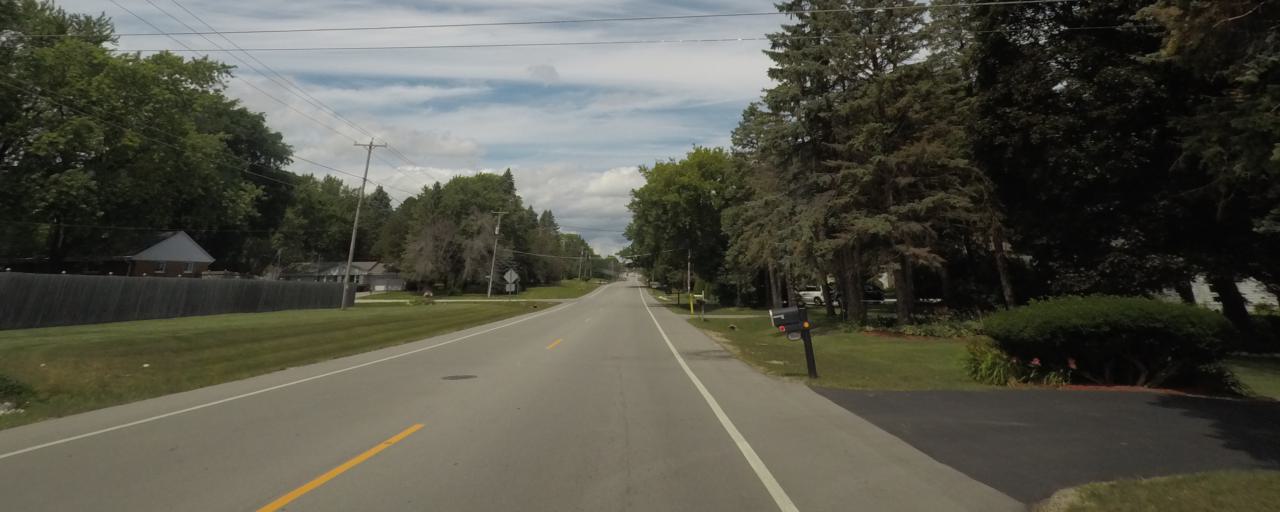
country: US
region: Wisconsin
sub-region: Waukesha County
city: New Berlin
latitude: 42.9890
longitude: -88.0683
